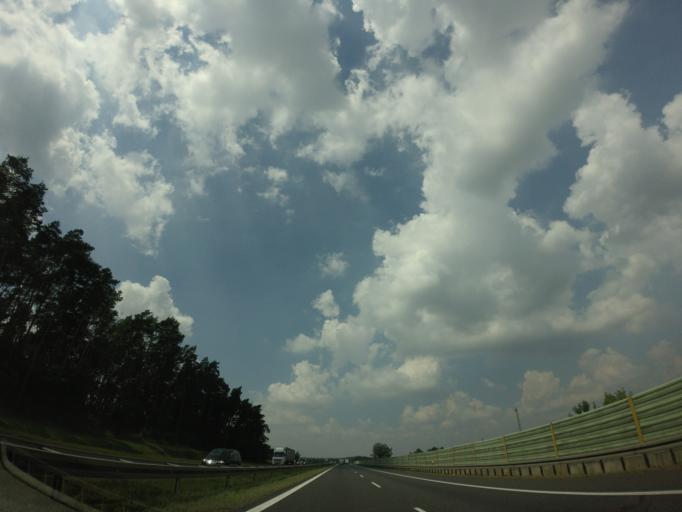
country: PL
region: Silesian Voivodeship
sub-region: Powiat gliwicki
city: Rudziniec
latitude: 50.3768
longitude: 18.4761
